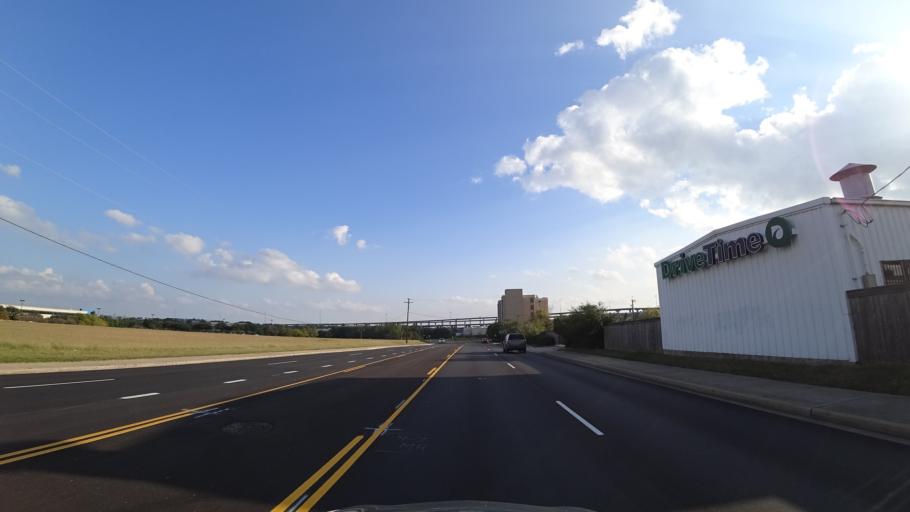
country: US
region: Texas
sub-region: Williamson County
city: Round Rock
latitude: 30.4886
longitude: -97.6741
